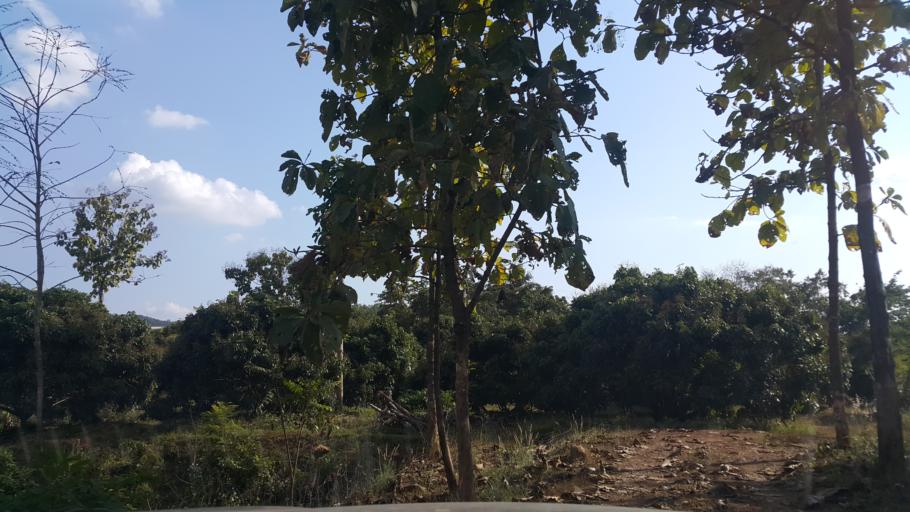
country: TH
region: Lamphun
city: Mae Tha
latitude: 18.5272
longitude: 99.1074
